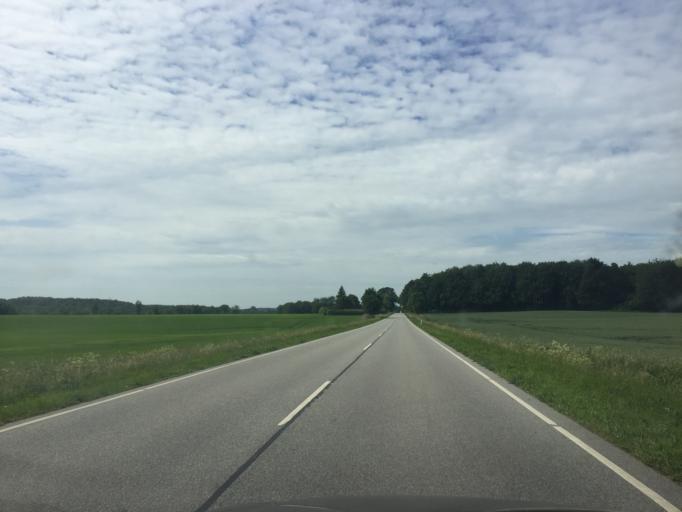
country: DK
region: South Denmark
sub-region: Nyborg Kommune
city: Ullerslev
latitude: 55.2438
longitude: 10.6579
